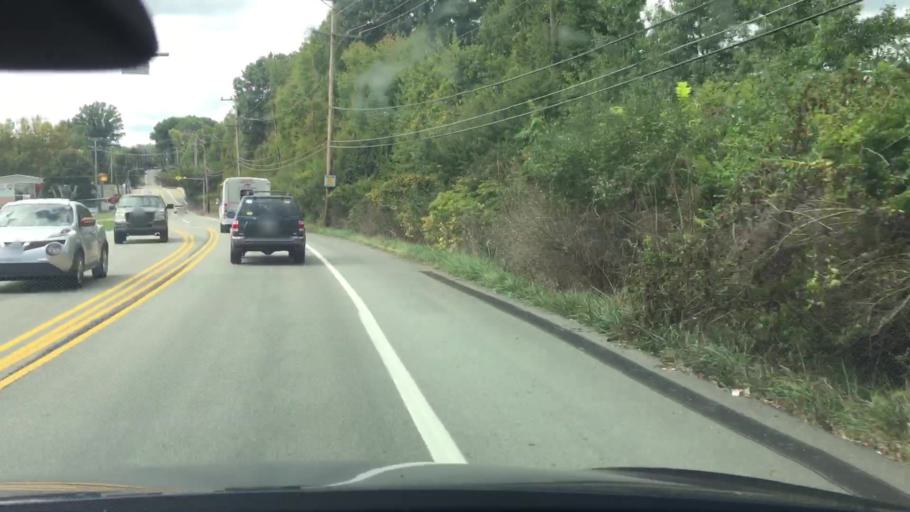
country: US
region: Pennsylvania
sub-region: Allegheny County
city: Cheswick
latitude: 40.5272
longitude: -79.8171
